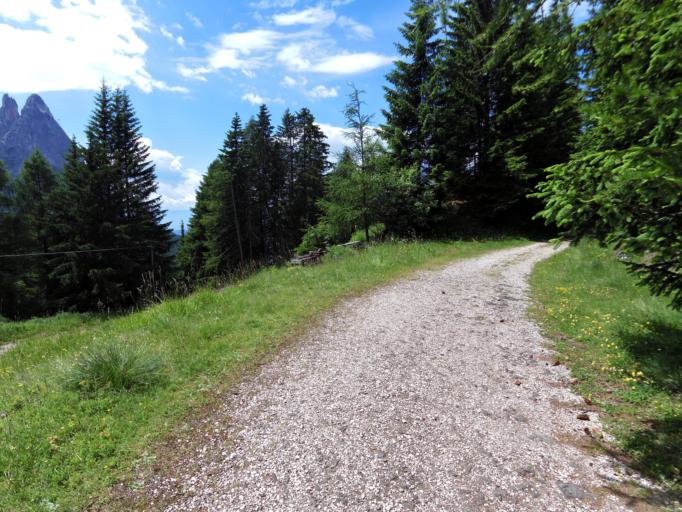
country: IT
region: Trentino-Alto Adige
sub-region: Bolzano
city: Siusi
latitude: 46.5385
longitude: 11.6012
